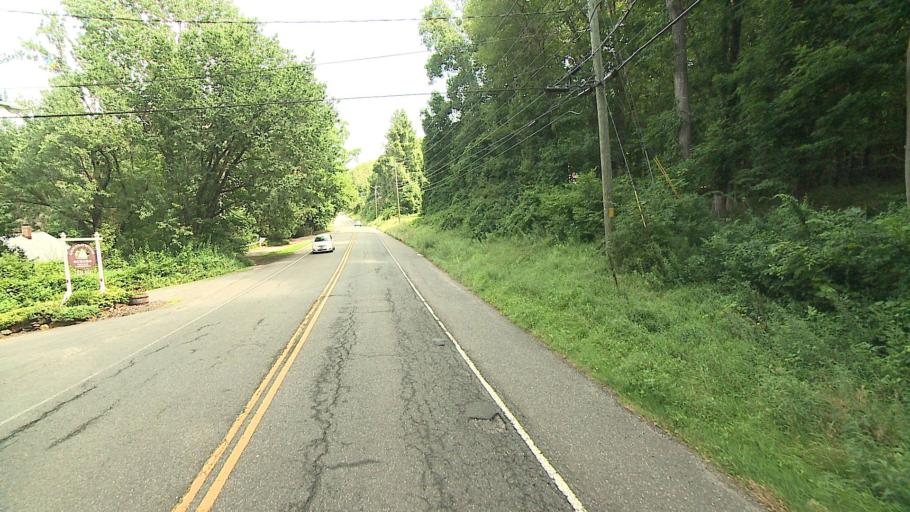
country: US
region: Connecticut
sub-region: Fairfield County
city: Sherman
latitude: 41.5333
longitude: -73.4790
